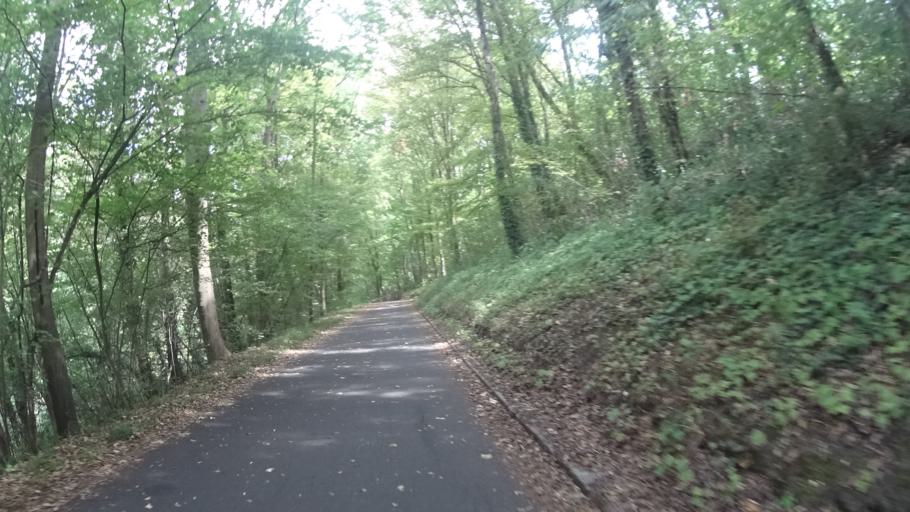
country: FR
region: Ile-de-France
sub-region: Departement de Seine-Saint-Denis
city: Tremblay-en-France
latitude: 48.9469
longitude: 2.5820
